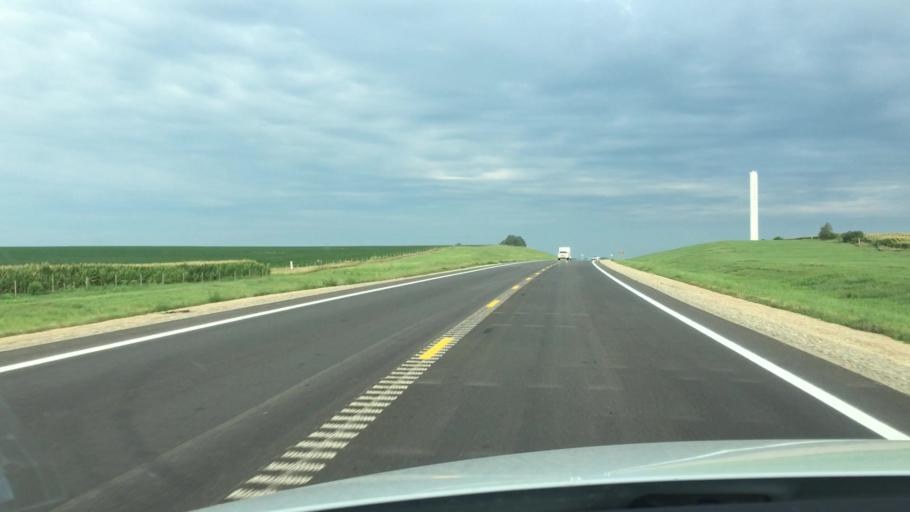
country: US
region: Kansas
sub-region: Doniphan County
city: Highland
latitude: 39.8421
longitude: -95.3432
